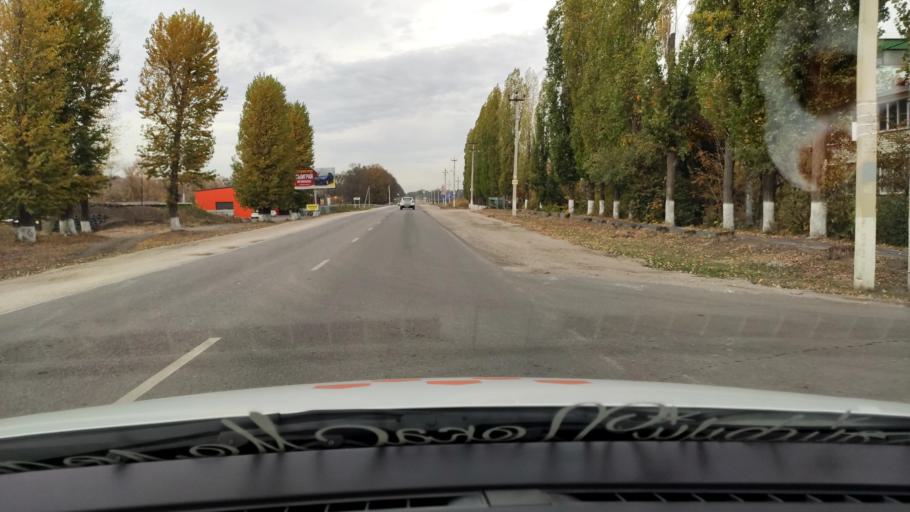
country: RU
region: Voronezj
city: Ramon'
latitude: 51.9182
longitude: 39.2943
